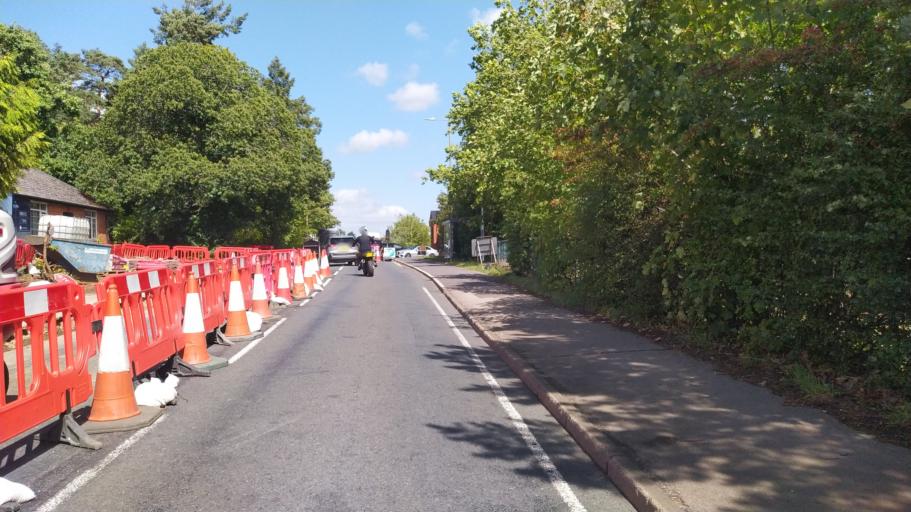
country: GB
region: England
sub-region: Hampshire
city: Bordon
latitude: 51.1170
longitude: -0.8605
